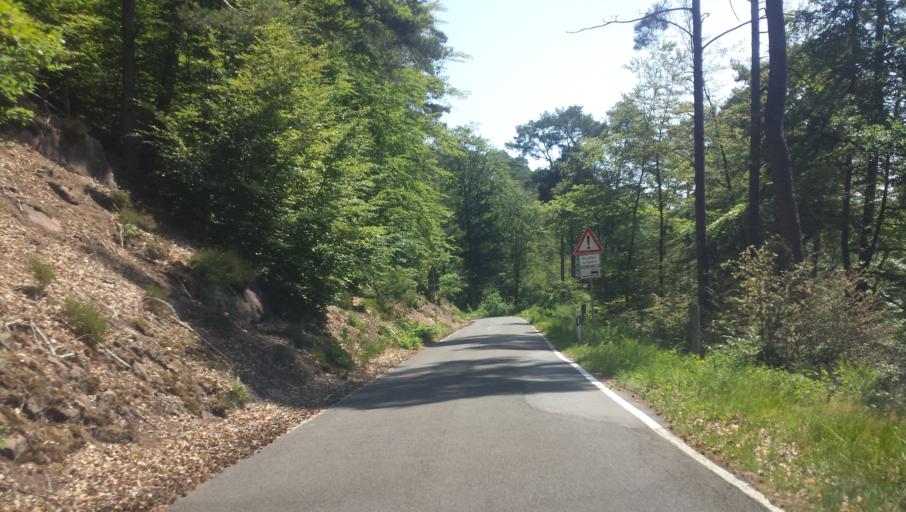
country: DE
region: Rheinland-Pfalz
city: Elmstein
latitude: 49.3613
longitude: 7.9132
